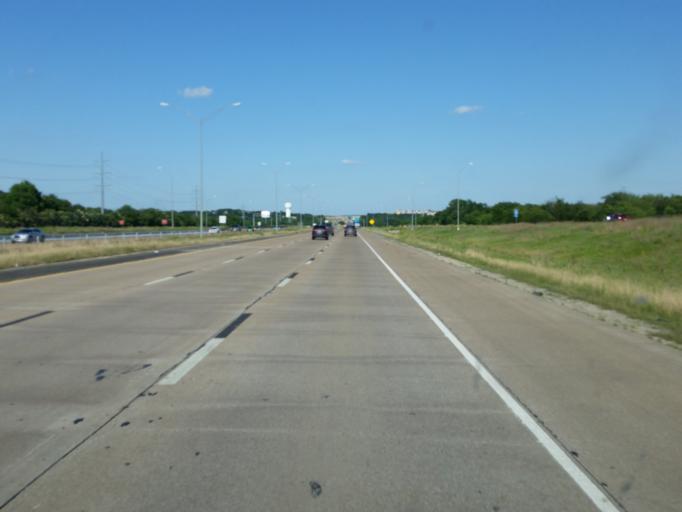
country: US
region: Texas
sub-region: Tarrant County
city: Benbrook
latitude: 32.6838
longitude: -97.4411
